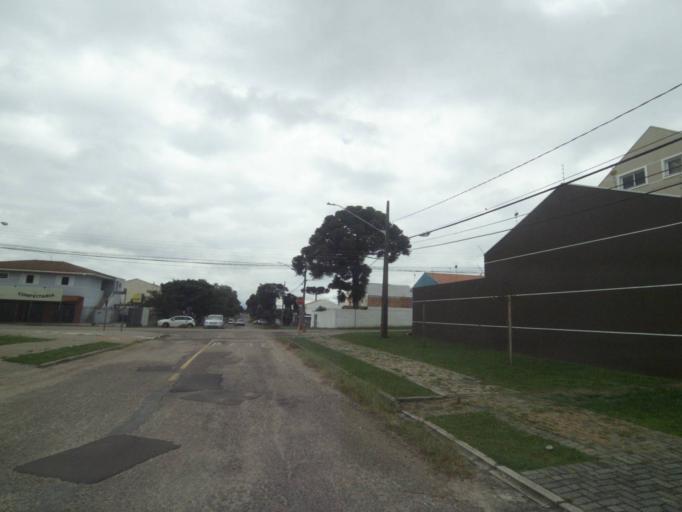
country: BR
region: Parana
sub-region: Pinhais
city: Pinhais
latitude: -25.4573
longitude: -49.2184
